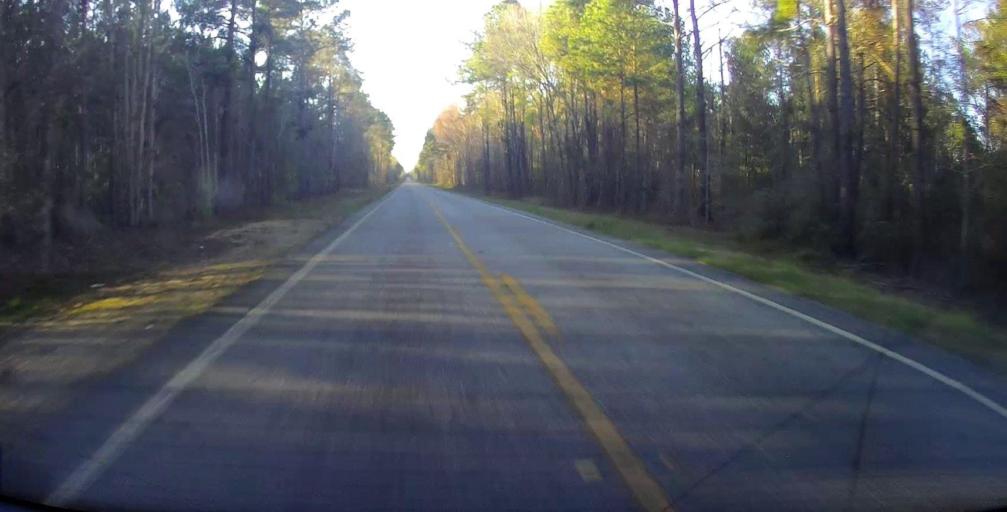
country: US
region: Georgia
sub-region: Wilcox County
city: Abbeville
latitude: 32.0887
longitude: -83.2936
